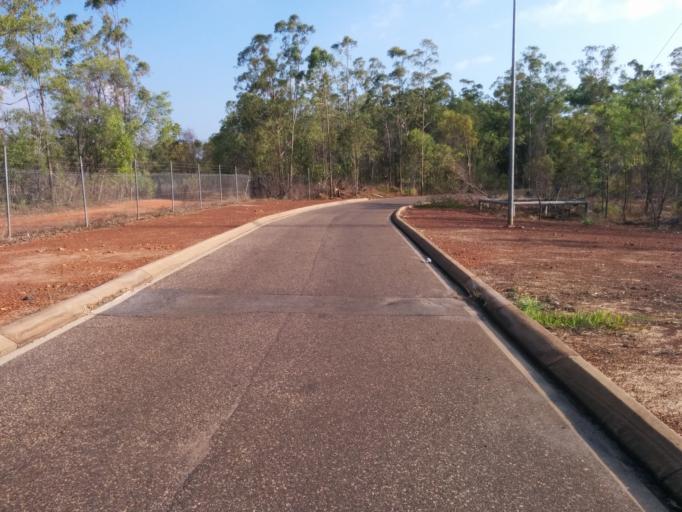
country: AU
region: Northern Territory
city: Alyangula
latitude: -13.8502
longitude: 136.4256
